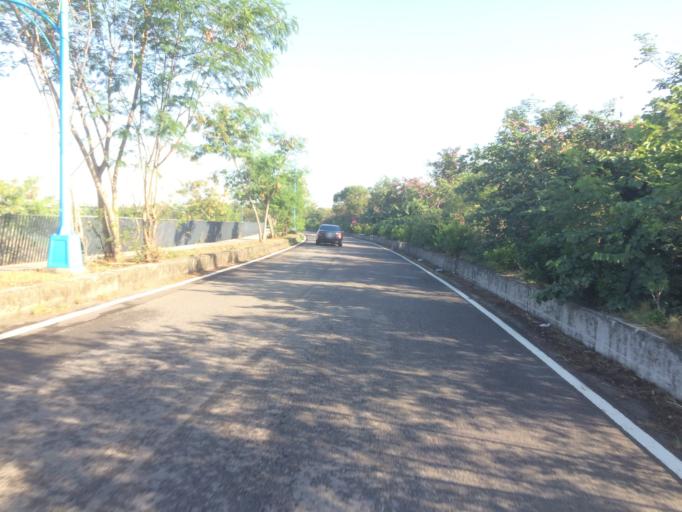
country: TW
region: Taiwan
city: Fengyuan
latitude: 24.1952
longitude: 120.7133
